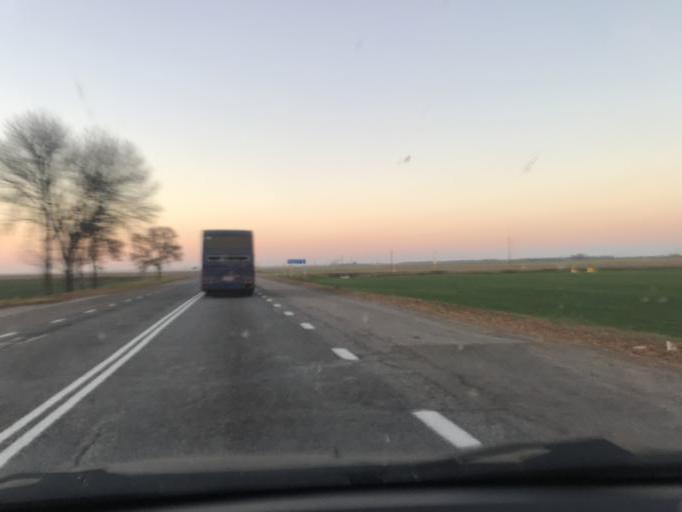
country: BY
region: Gomel
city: Horad Rechytsa
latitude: 52.2218
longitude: 30.5197
